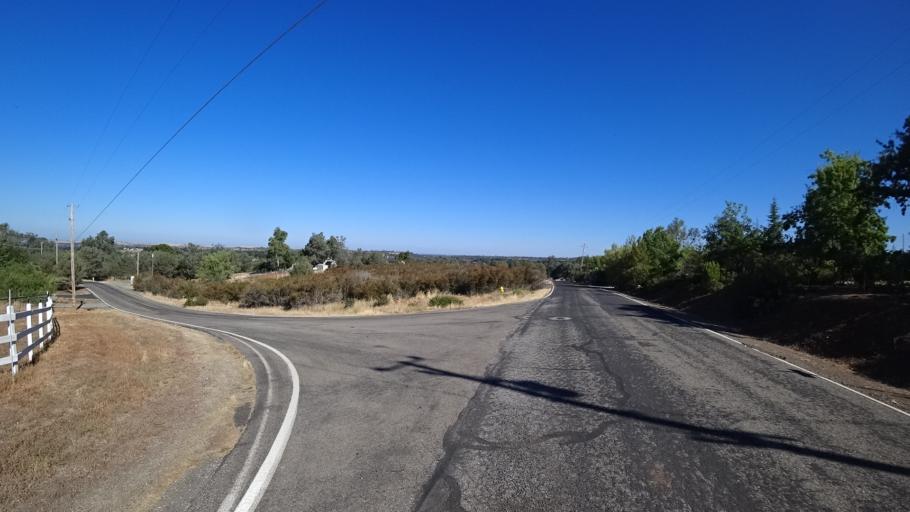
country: US
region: California
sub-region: Calaveras County
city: Rancho Calaveras
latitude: 38.1143
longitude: -120.8522
